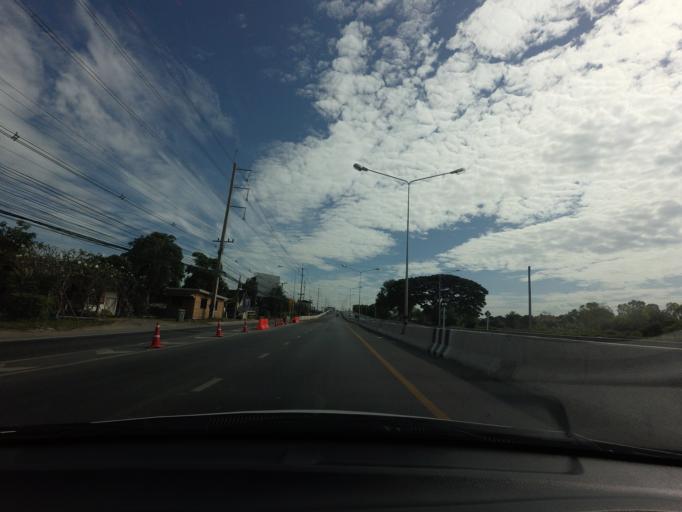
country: TH
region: Pathum Thani
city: Nong Suea
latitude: 14.0755
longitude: 100.8888
